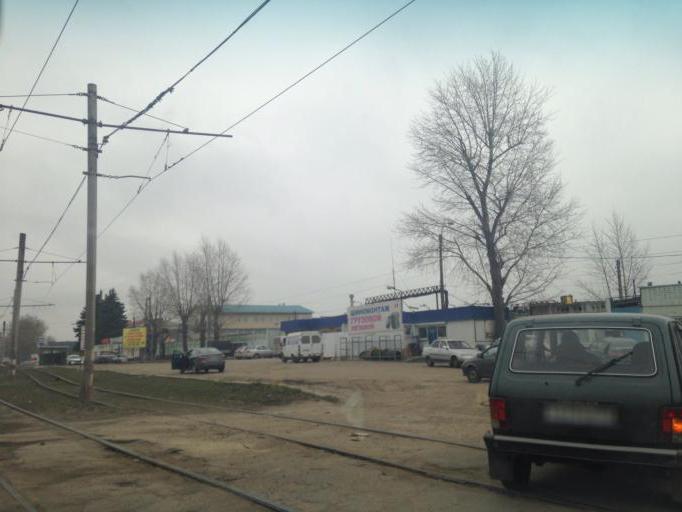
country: RU
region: Ulyanovsk
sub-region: Ulyanovskiy Rayon
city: Ulyanovsk
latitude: 54.3036
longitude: 48.3022
